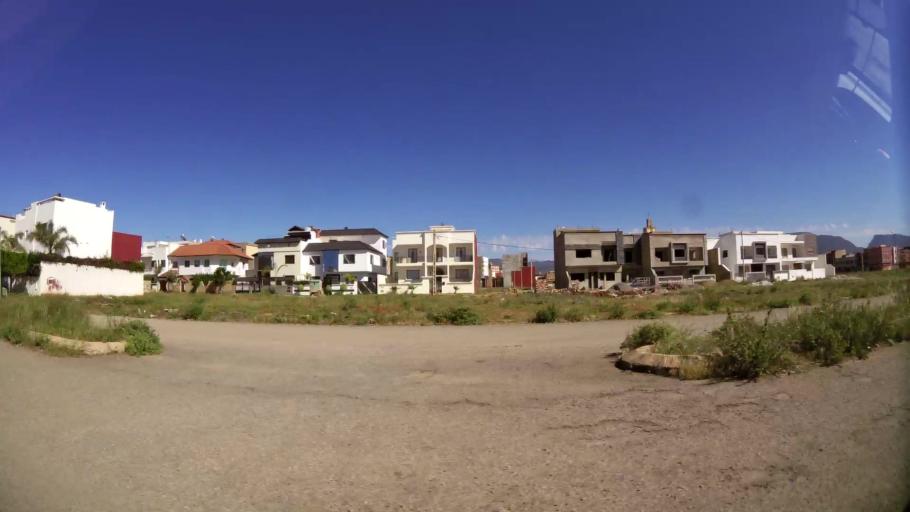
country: MA
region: Oriental
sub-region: Berkane-Taourirt
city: Berkane
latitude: 34.9429
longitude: -2.3349
